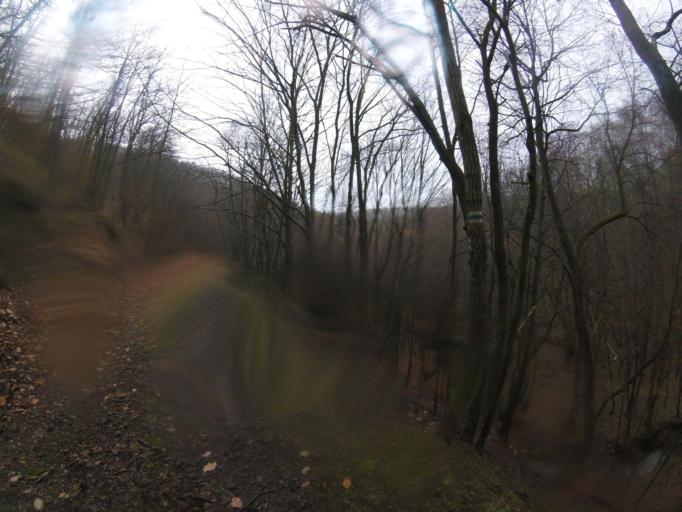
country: HU
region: Pest
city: Szob
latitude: 47.8644
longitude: 18.8492
